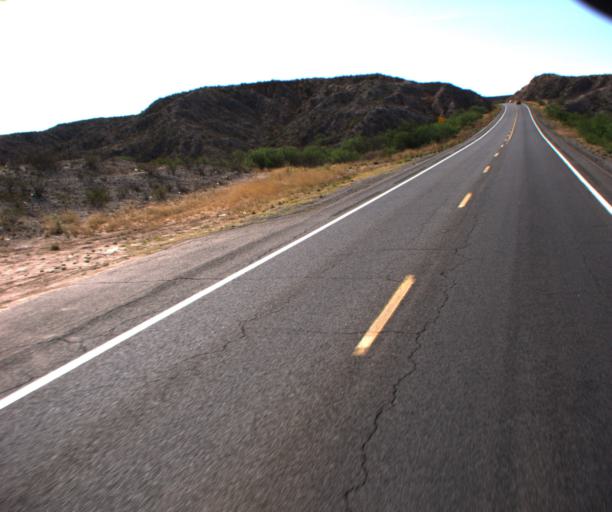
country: US
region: Arizona
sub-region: Cochise County
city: Saint David
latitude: 31.8245
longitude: -110.1759
